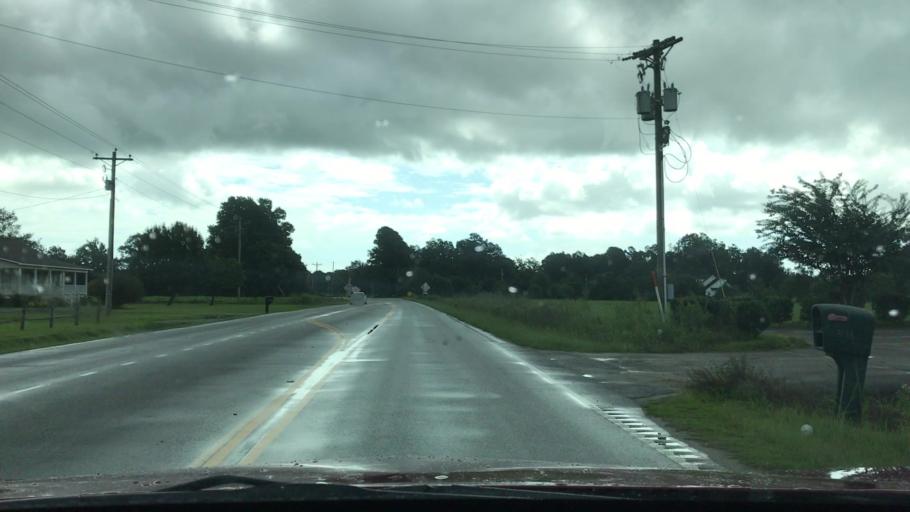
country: US
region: South Carolina
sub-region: Horry County
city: Loris
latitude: 33.9049
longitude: -78.8396
